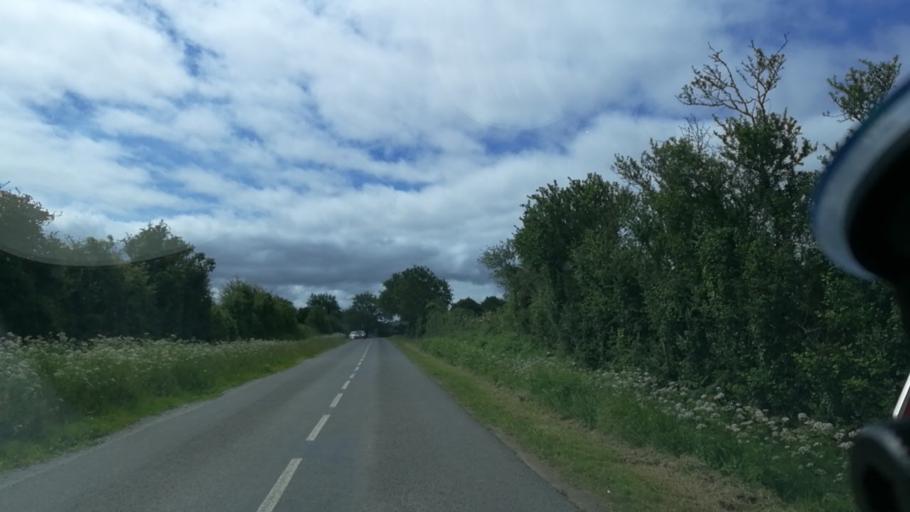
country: FR
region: Brittany
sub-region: Departement du Morbihan
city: Penestin
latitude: 47.4690
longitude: -2.4315
